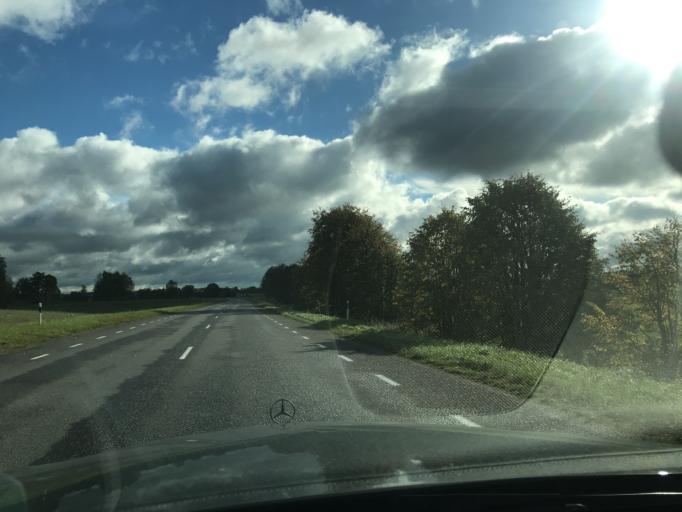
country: EE
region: Valgamaa
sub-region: Torva linn
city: Torva
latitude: 57.9790
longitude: 25.9715
